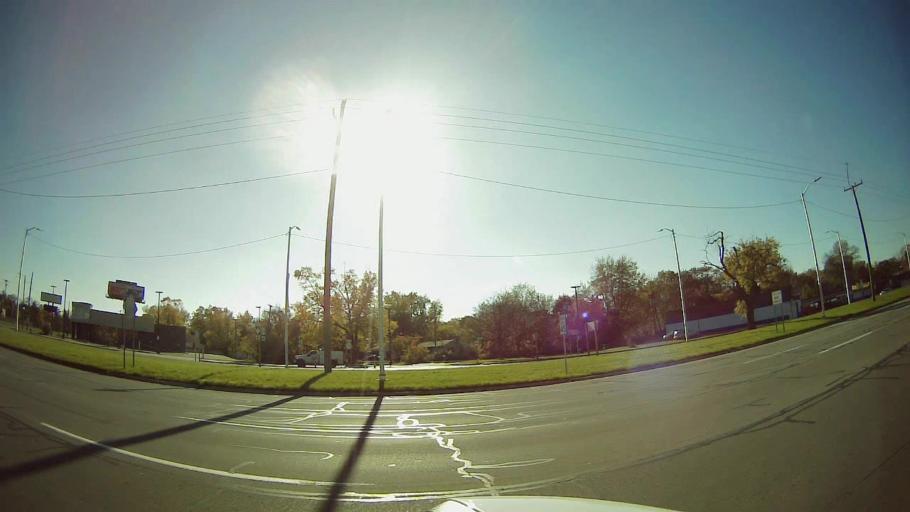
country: US
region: Michigan
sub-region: Wayne County
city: Redford
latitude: 42.4251
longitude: -83.2784
